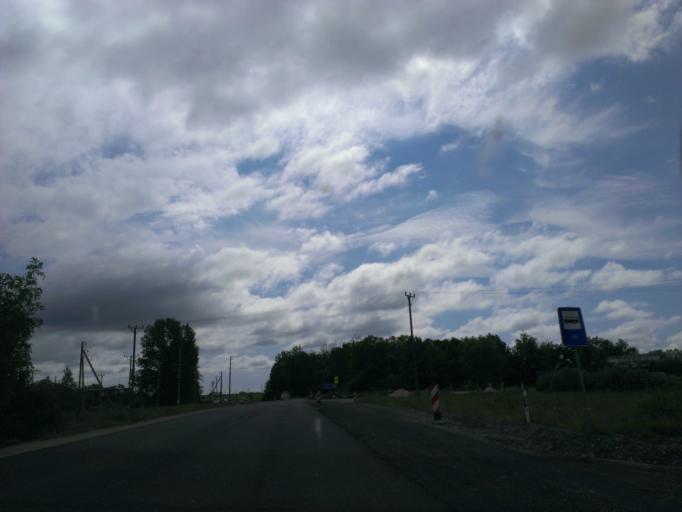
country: LV
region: Durbe
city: Liegi
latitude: 56.5666
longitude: 21.2730
